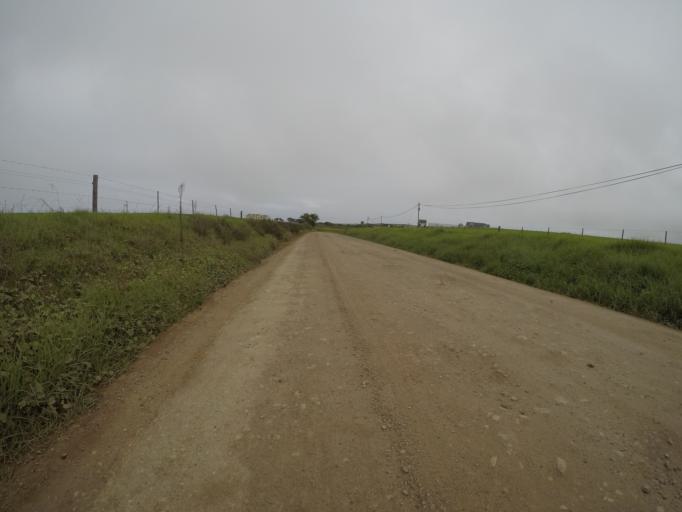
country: ZA
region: Eastern Cape
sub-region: Cacadu District Municipality
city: Kareedouw
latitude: -34.0696
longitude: 24.2372
